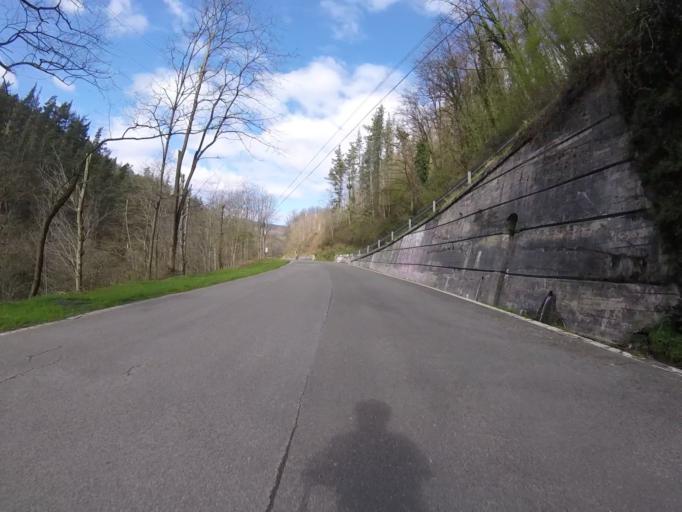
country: ES
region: Navarre
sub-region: Provincia de Navarra
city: Goizueta
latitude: 43.1634
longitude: -1.8526
